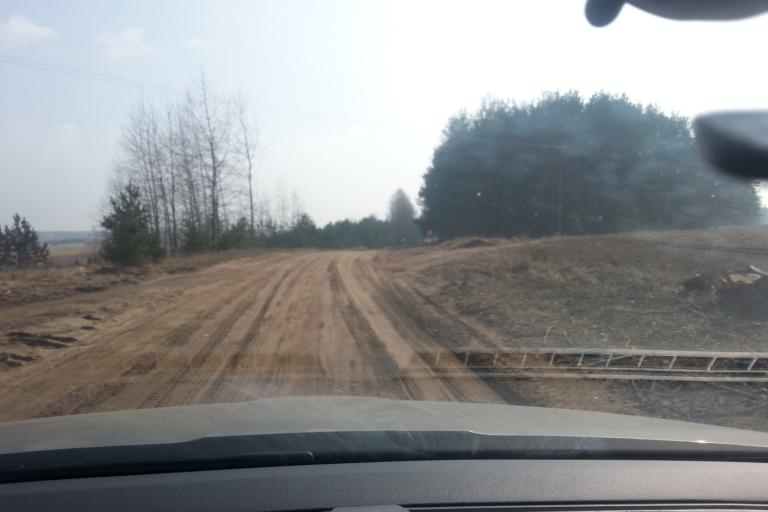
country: LT
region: Vilnius County
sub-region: Trakai
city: Rudiskes
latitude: 54.5051
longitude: 24.9539
